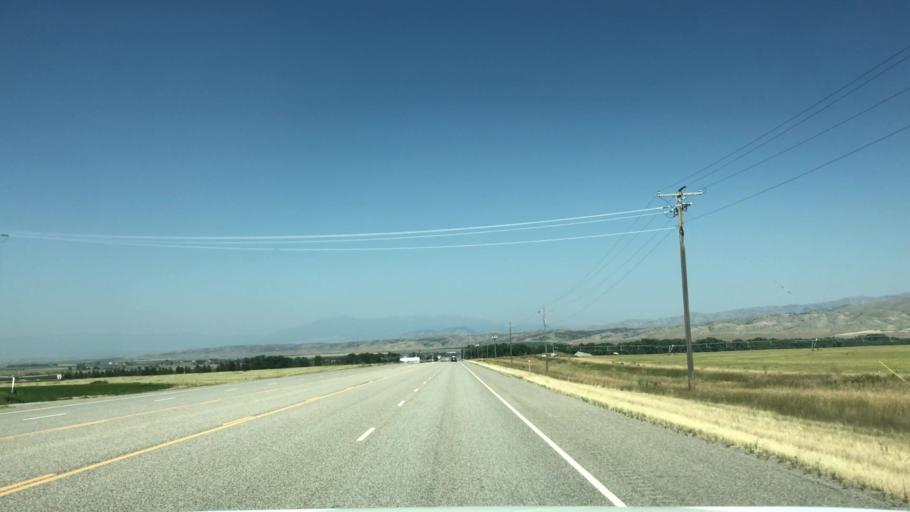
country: US
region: Montana
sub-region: Broadwater County
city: Townsend
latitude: 46.1451
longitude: -111.4737
